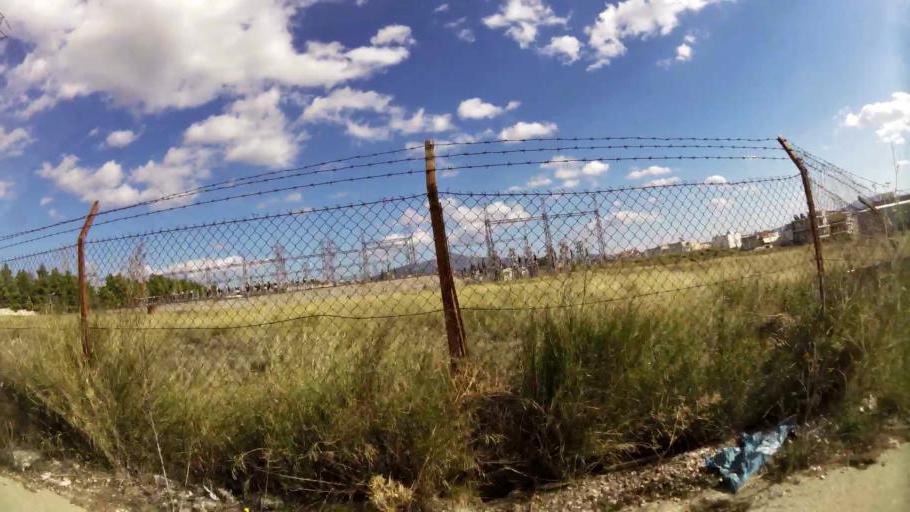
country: GR
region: Attica
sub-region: Nomarchia Anatolikis Attikis
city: Acharnes
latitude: 38.0997
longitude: 23.7326
